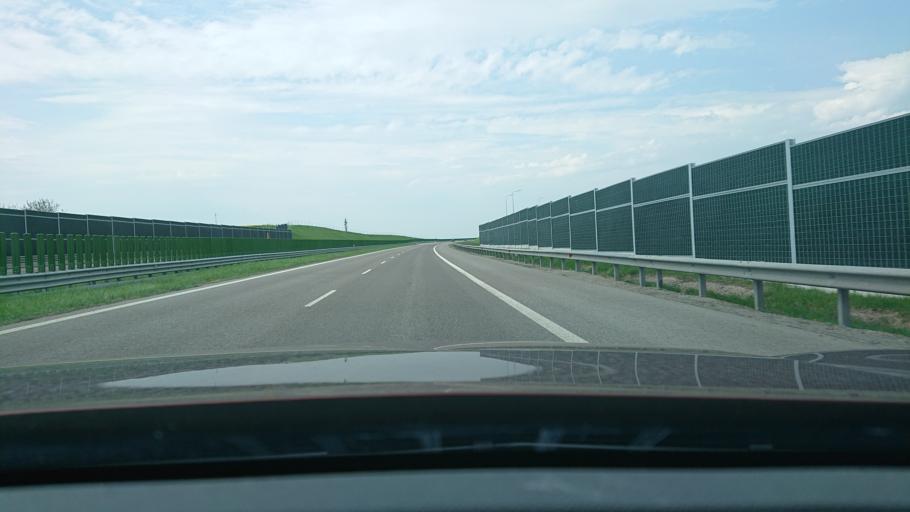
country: PL
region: Subcarpathian Voivodeship
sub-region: Powiat jaroslawski
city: Rokietnica
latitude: 49.9448
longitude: 22.6682
